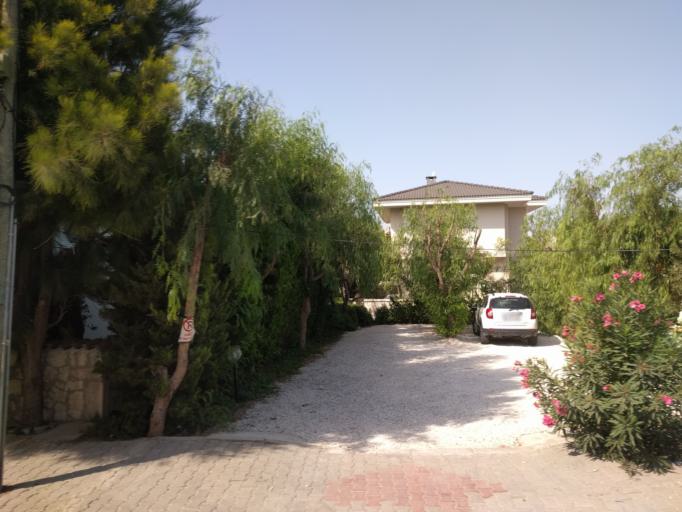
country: TR
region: Izmir
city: Alacati
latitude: 38.3038
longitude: 26.3655
